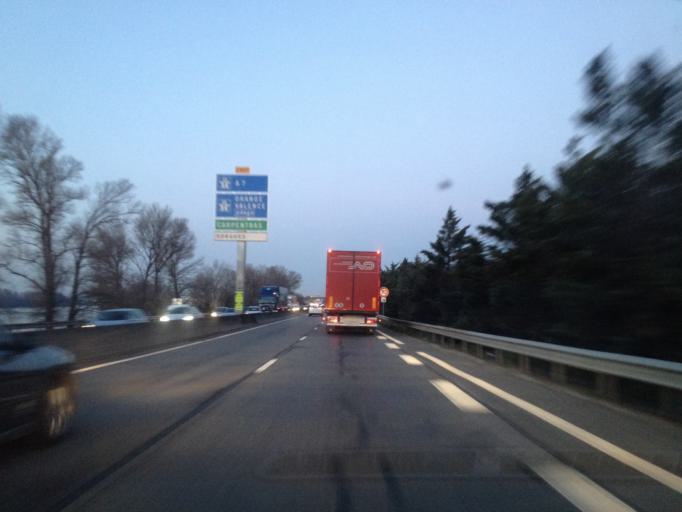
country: FR
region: Provence-Alpes-Cote d'Azur
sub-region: Departement du Vaucluse
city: Le Pontet
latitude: 43.9663
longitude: 4.8539
